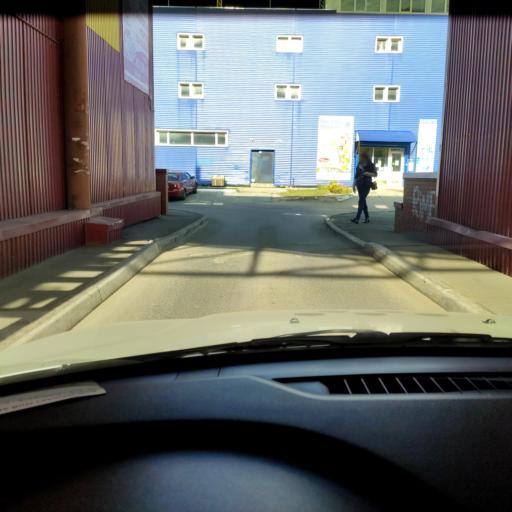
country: RU
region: Samara
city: Tol'yatti
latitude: 53.5385
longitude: 49.3623
